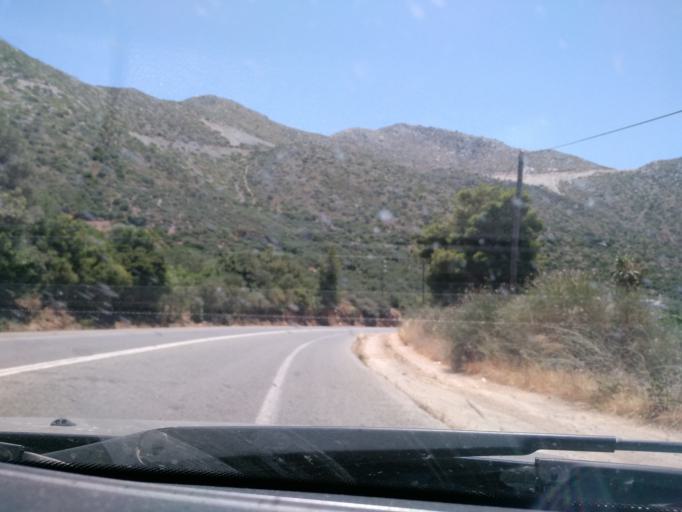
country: GR
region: Crete
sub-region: Nomos Rethymnis
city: Anogeia
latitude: 35.3884
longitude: 24.8868
